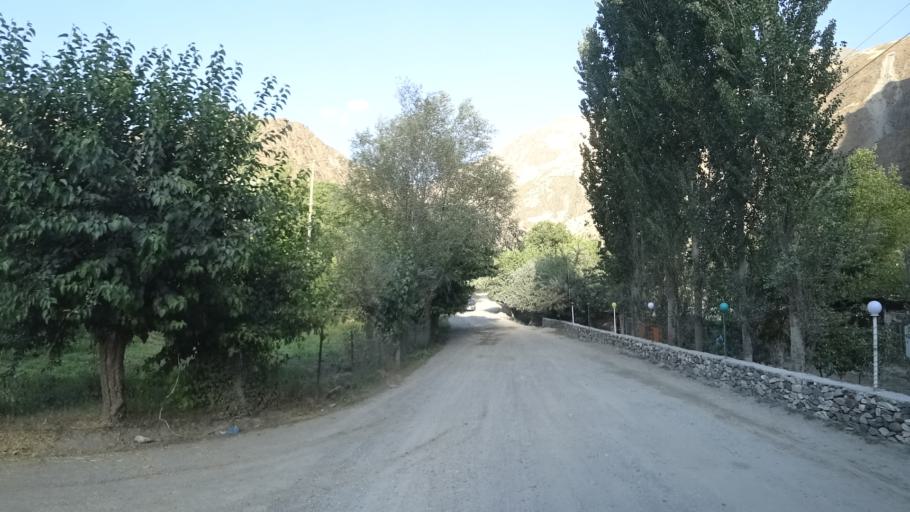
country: AF
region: Badakhshan
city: Maymay
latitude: 38.4781
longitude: 70.9590
